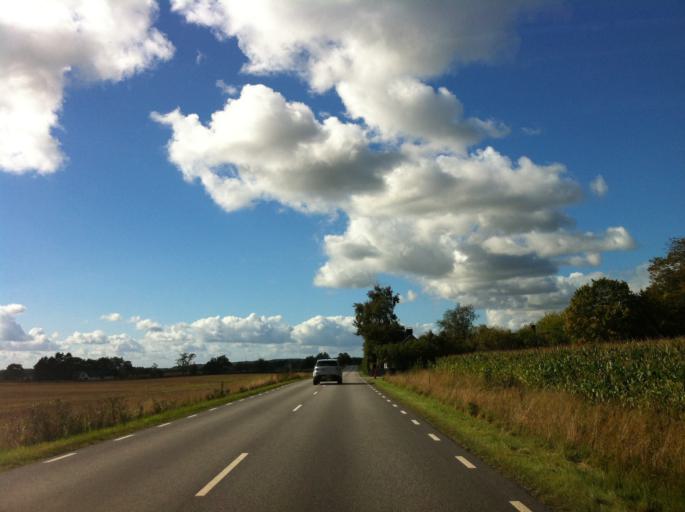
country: SE
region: Skane
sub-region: Tomelilla Kommun
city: Tomelilla
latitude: 55.6541
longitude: 13.9325
